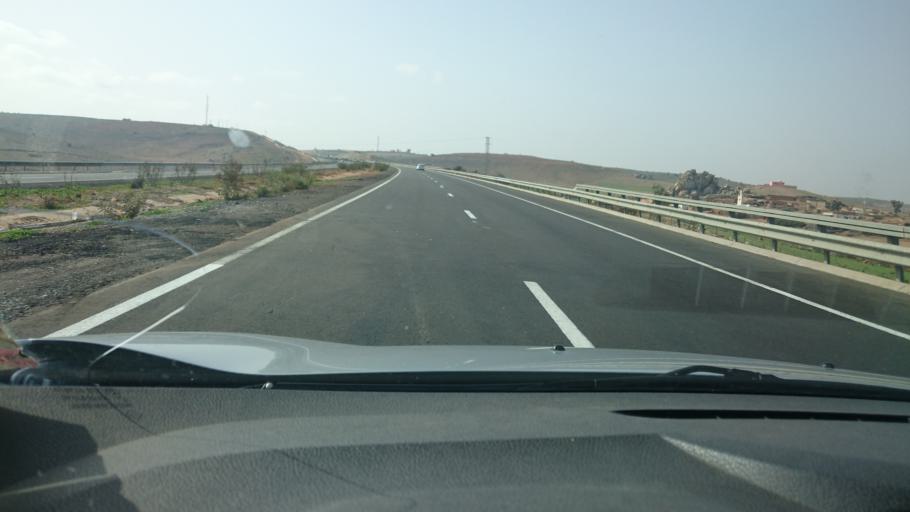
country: MA
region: Marrakech-Tensift-Al Haouz
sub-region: Kelaa-Des-Sraghna
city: Sidi Abdallah
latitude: 32.5439
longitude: -7.9013
